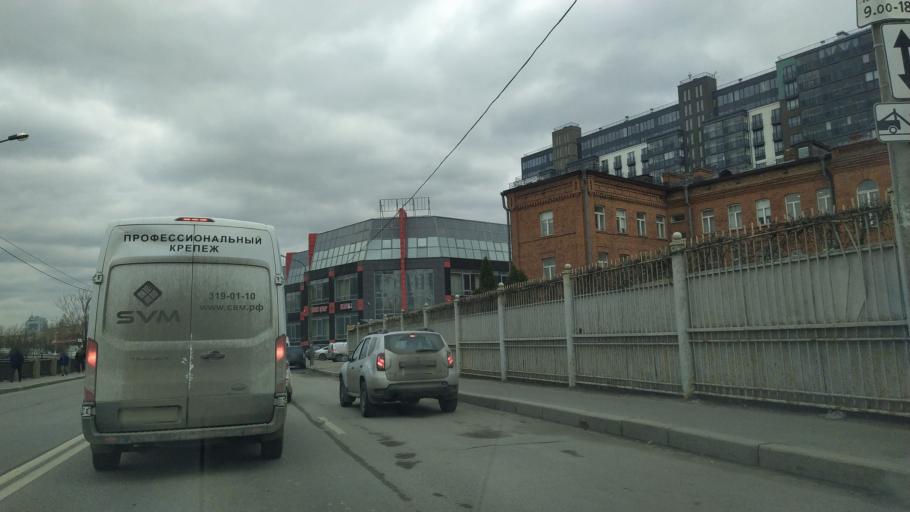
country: RU
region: St.-Petersburg
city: Centralniy
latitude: 59.9354
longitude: 30.4156
